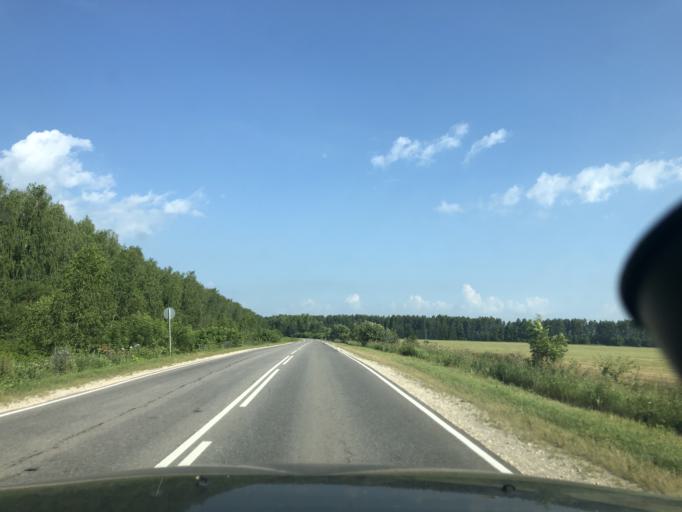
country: RU
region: Tula
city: Dubna
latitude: 54.1191
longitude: 37.0786
